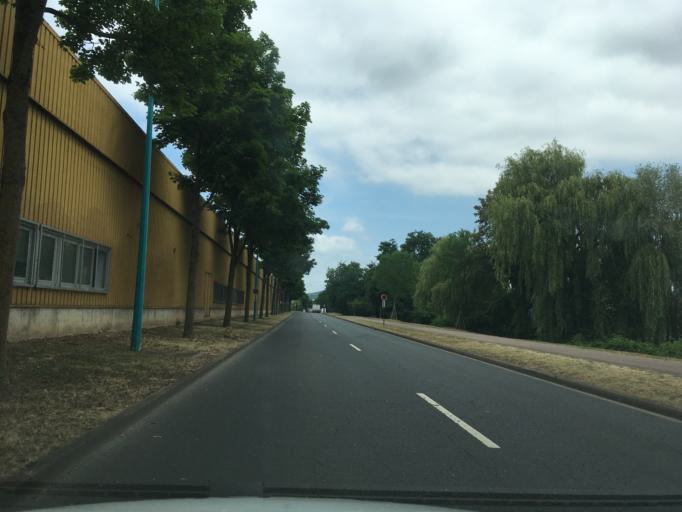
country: FR
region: Lorraine
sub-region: Departement de Meurthe-et-Moselle
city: Tomblaine
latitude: 48.6798
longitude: 6.2075
